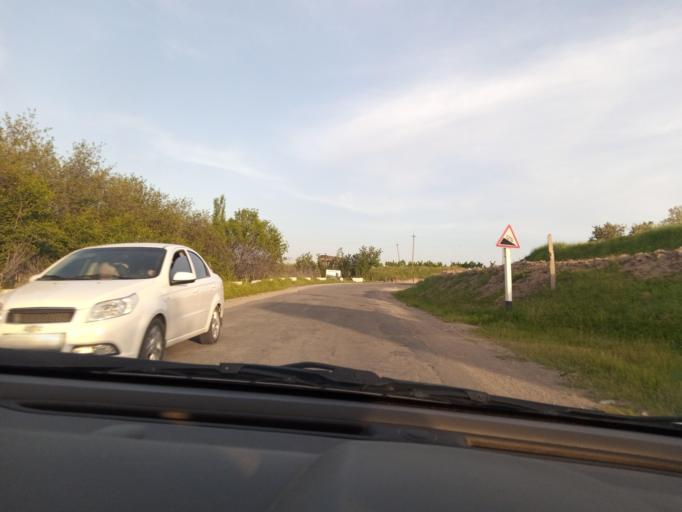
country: UZ
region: Toshkent
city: Parkent
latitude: 41.2363
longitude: 69.7365
